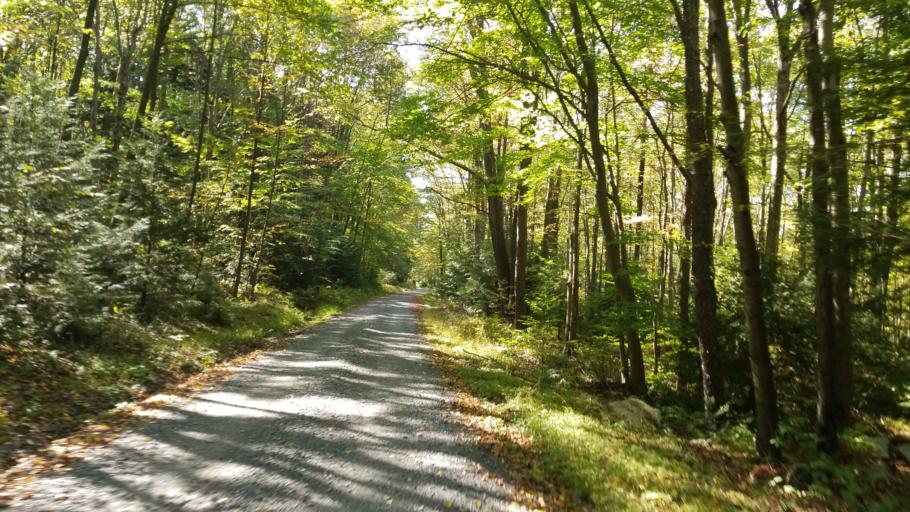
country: US
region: Pennsylvania
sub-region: Clearfield County
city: Clearfield
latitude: 41.1867
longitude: -78.5066
